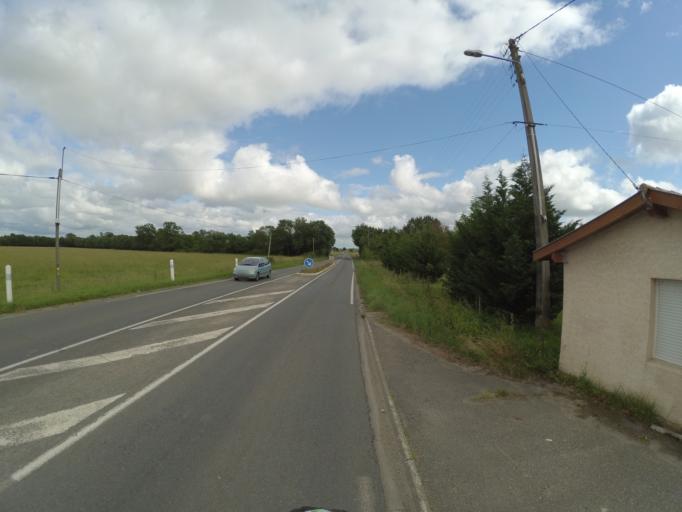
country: FR
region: Aquitaine
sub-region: Departement de la Gironde
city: Ludon-Medoc
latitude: 44.9810
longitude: -0.5644
